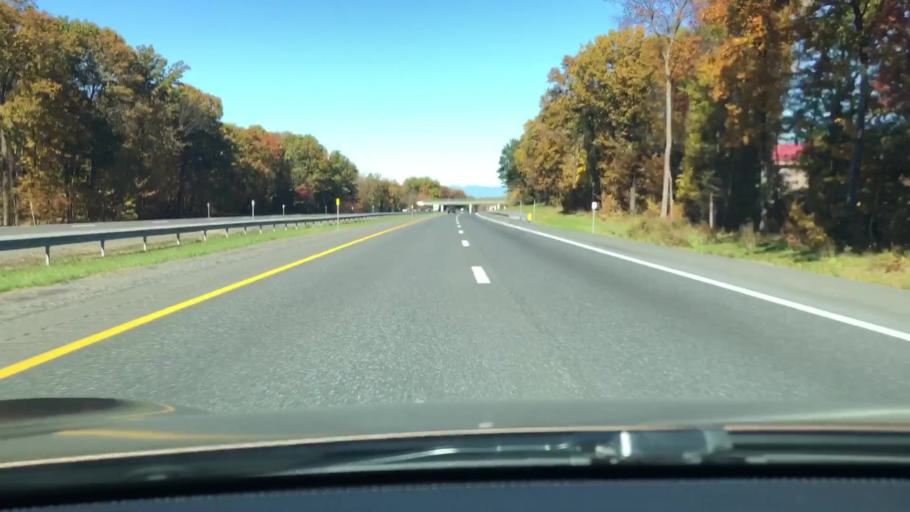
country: US
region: New York
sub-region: Ulster County
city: Plattekill
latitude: 41.6565
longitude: -74.0780
